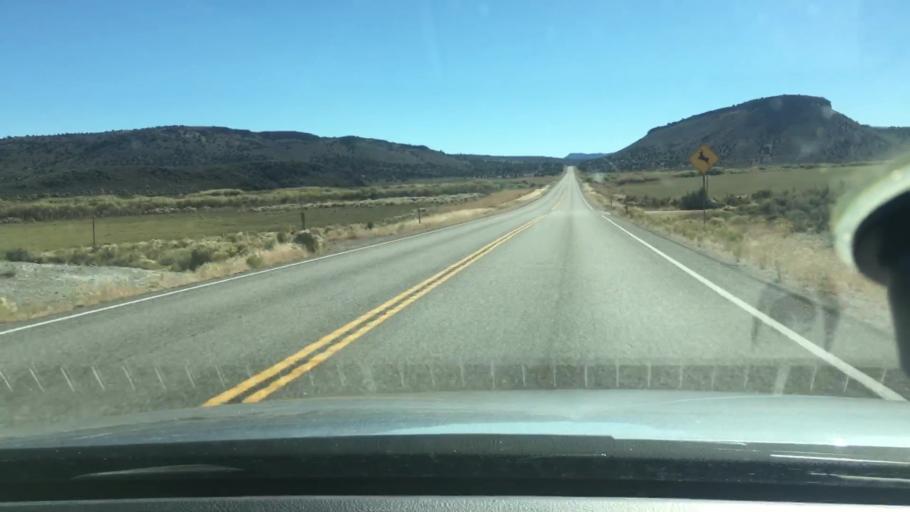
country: US
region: Nevada
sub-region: White Pine County
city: Ely
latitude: 38.9308
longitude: -115.1746
